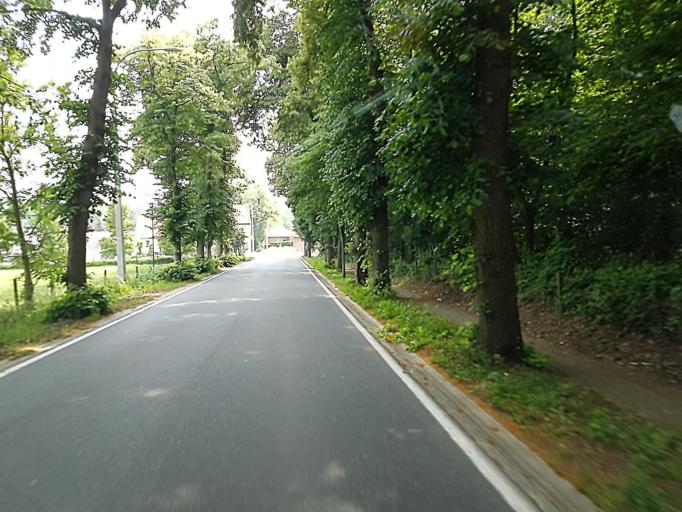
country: BE
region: Flanders
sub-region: Provincie West-Vlaanderen
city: Anzegem
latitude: 50.8151
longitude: 3.4684
